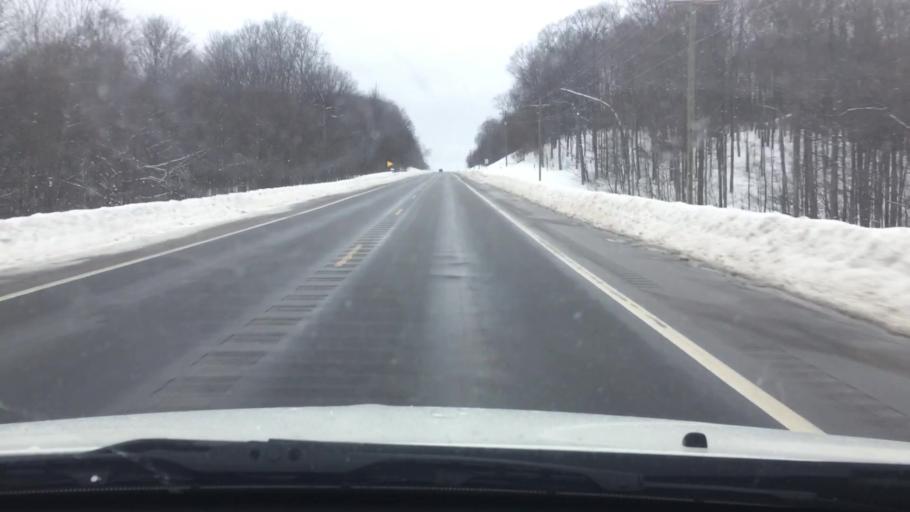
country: US
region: Michigan
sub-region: Charlevoix County
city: Boyne City
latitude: 45.0963
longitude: -85.0042
